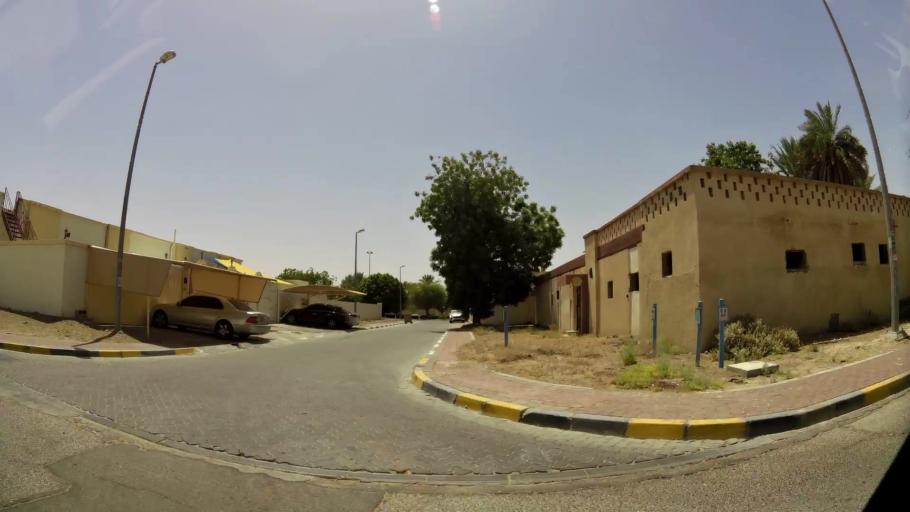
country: OM
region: Al Buraimi
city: Al Buraymi
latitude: 24.2800
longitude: 55.7630
